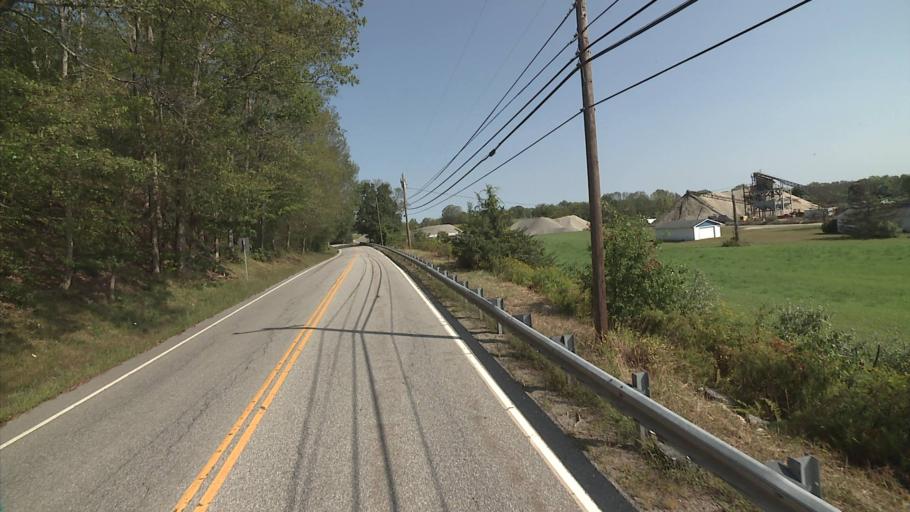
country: US
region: Connecticut
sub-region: Windham County
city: Plainfield Village
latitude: 41.6728
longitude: -71.9724
